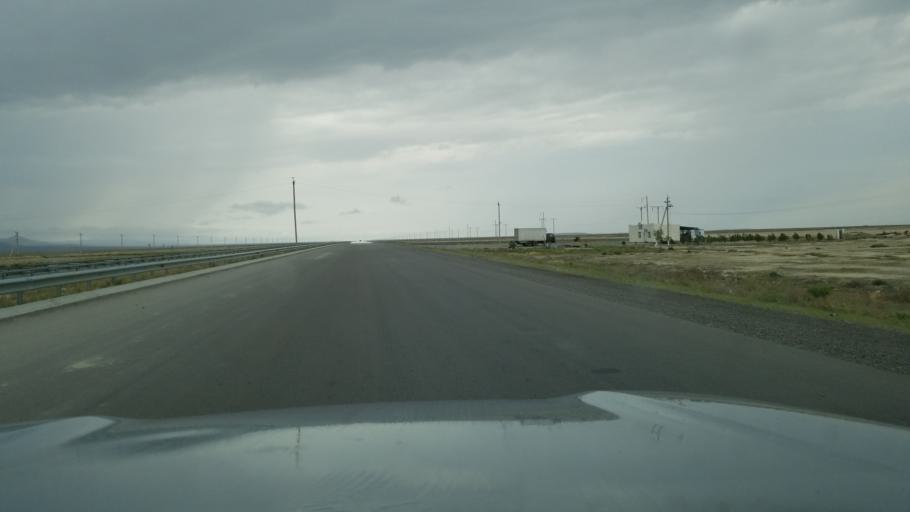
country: TM
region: Balkan
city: Serdar
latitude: 39.0440
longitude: 56.1465
